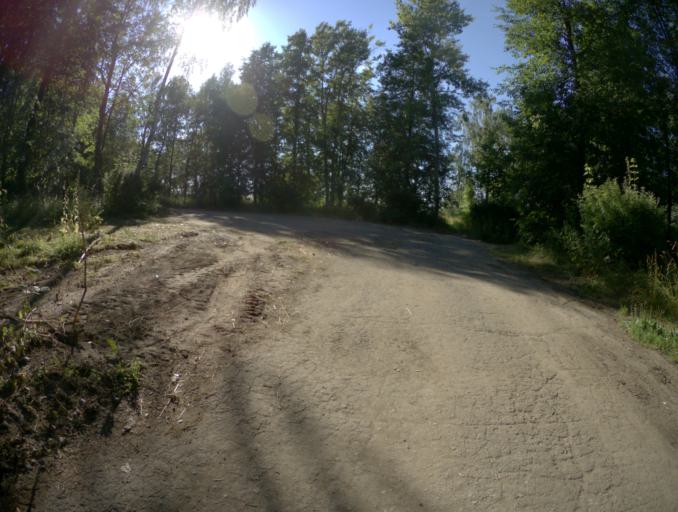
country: RU
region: Nizjnij Novgorod
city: Taremskoye
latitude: 55.9617
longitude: 43.0511
